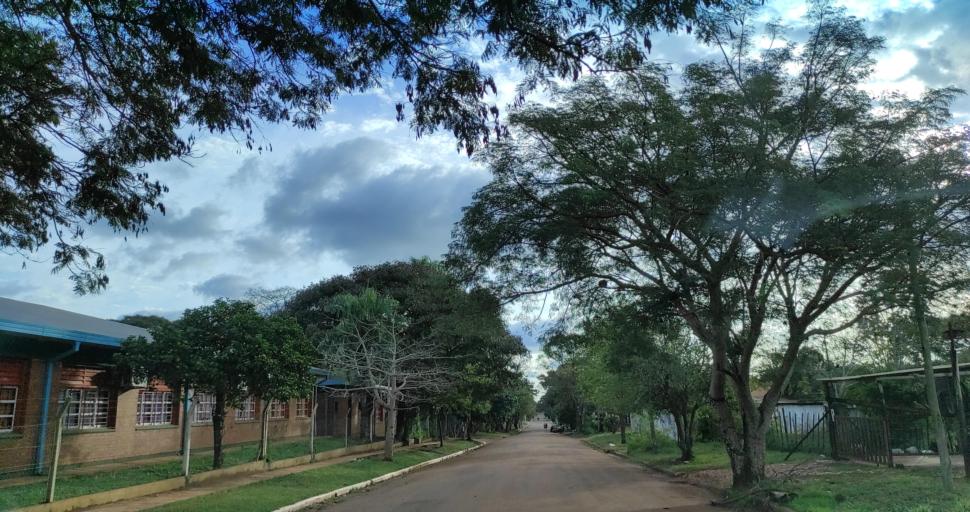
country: AR
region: Misiones
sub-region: Departamento de Candelaria
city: Candelaria
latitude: -27.4598
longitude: -55.7412
